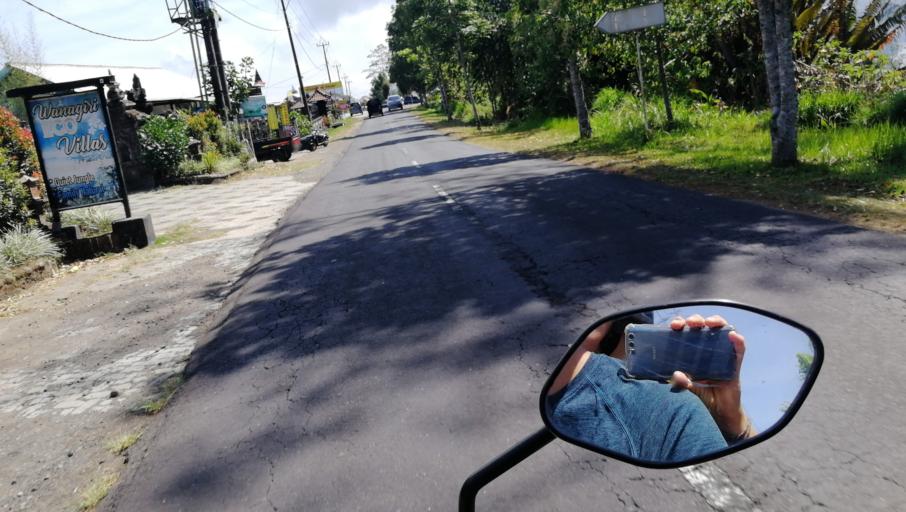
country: ID
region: Bali
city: Munduk
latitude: -8.2412
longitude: 115.1062
